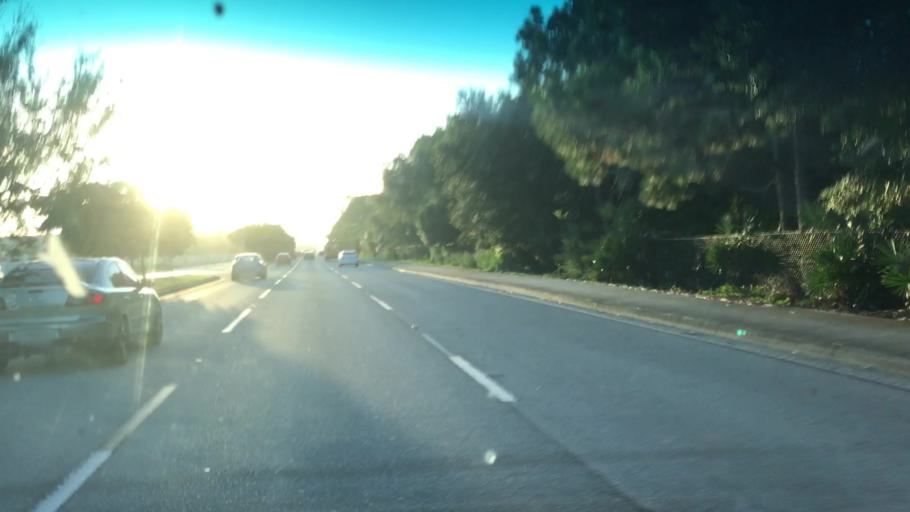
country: US
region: Florida
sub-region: Lee County
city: Villas
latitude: 26.5460
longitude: -81.8797
